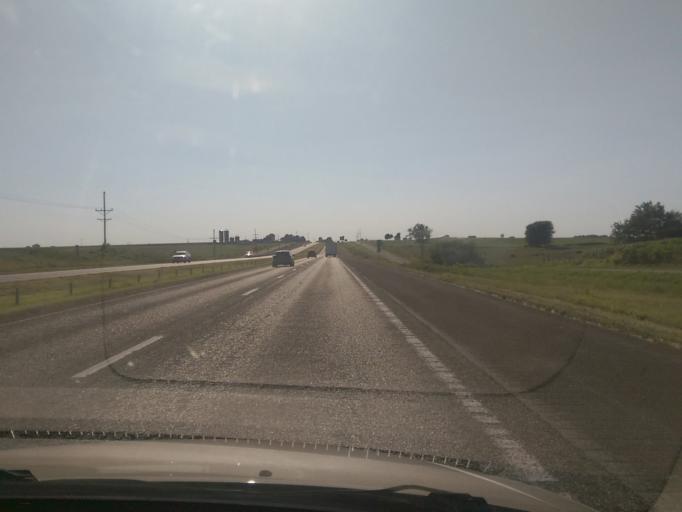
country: US
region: Missouri
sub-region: Lafayette County
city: Concordia
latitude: 38.9887
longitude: -93.5373
